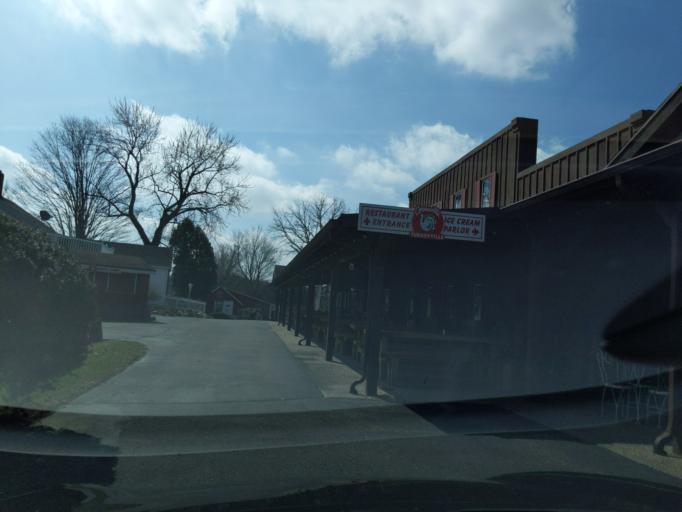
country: US
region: Michigan
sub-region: Calhoun County
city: Marshall
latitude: 42.3476
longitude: -84.9964
